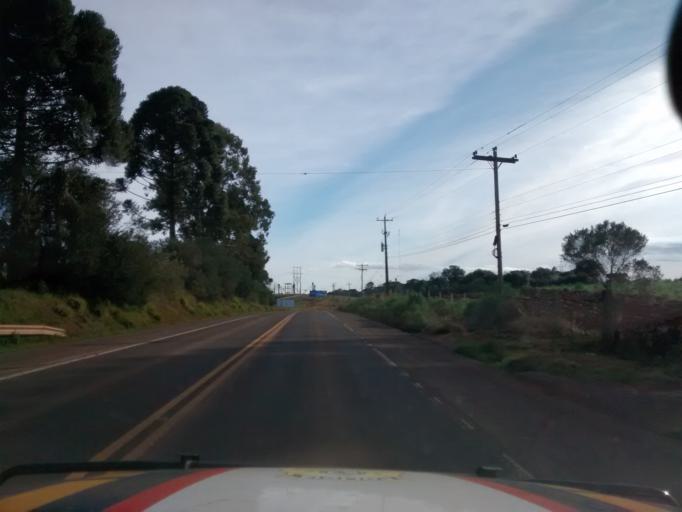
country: BR
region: Rio Grande do Sul
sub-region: Lagoa Vermelha
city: Lagoa Vermelha
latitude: -28.1928
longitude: -51.5258
